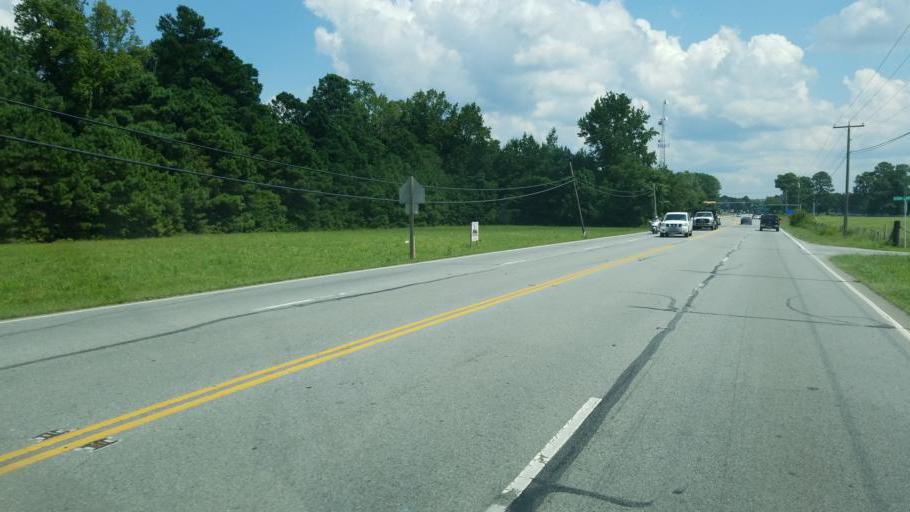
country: US
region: Virginia
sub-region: City of Suffolk
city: Suffolk
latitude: 36.7729
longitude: -76.6131
